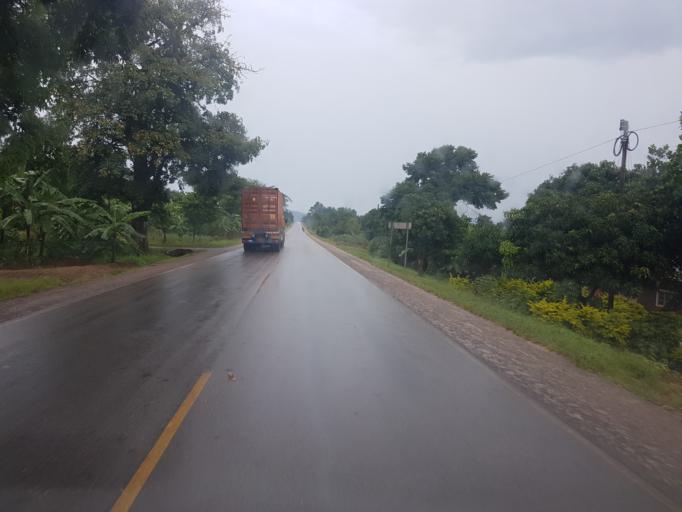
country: UG
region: Central Region
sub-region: Butambala District
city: Gombe
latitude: 0.0748
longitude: 32.1220
